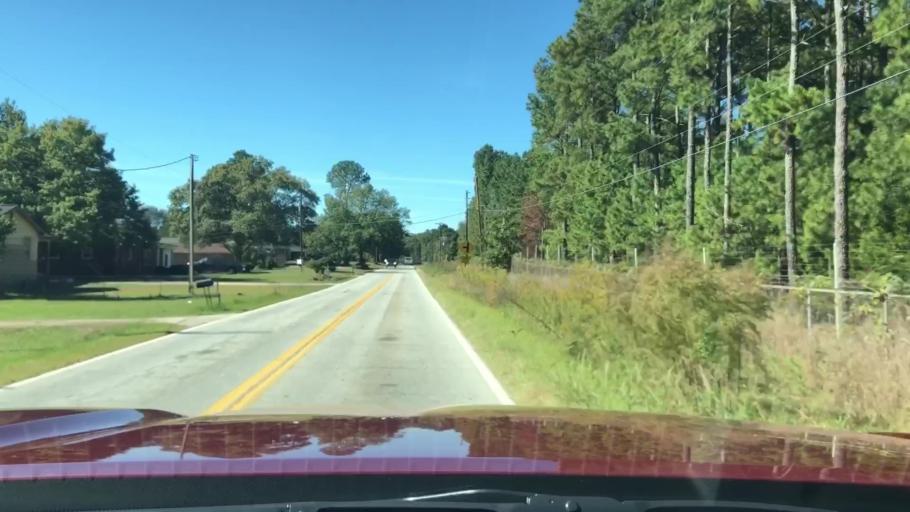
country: US
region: South Carolina
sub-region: Greenwood County
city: Greenwood
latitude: 34.2213
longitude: -82.1271
